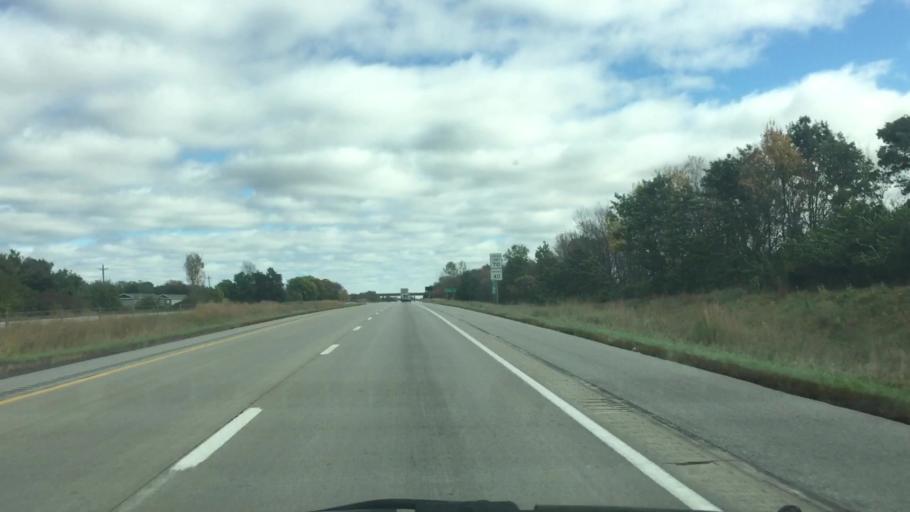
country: US
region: Iowa
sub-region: Jasper County
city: Newton
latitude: 41.6837
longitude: -93.0651
